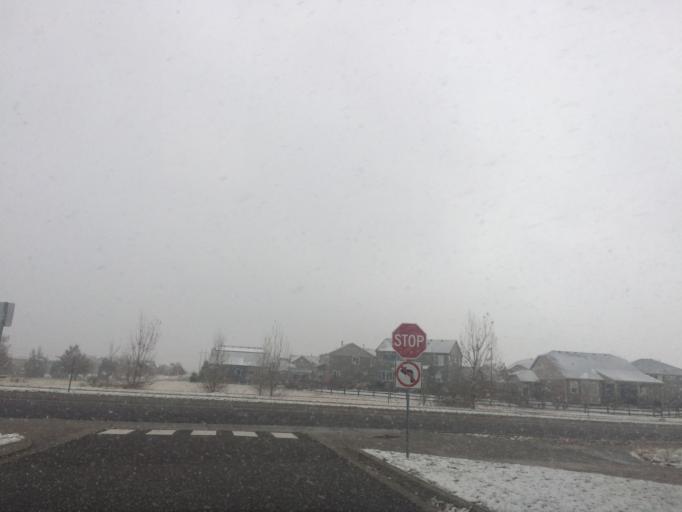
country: US
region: Colorado
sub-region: Boulder County
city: Erie
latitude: 40.0437
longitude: -105.0654
